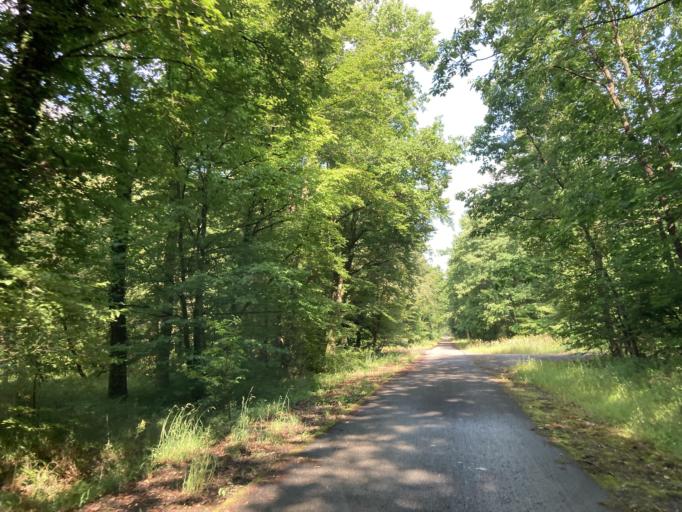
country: DE
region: Baden-Wuerttemberg
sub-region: Karlsruhe Region
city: Karlsdorf-Neuthard
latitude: 49.1586
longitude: 8.5223
